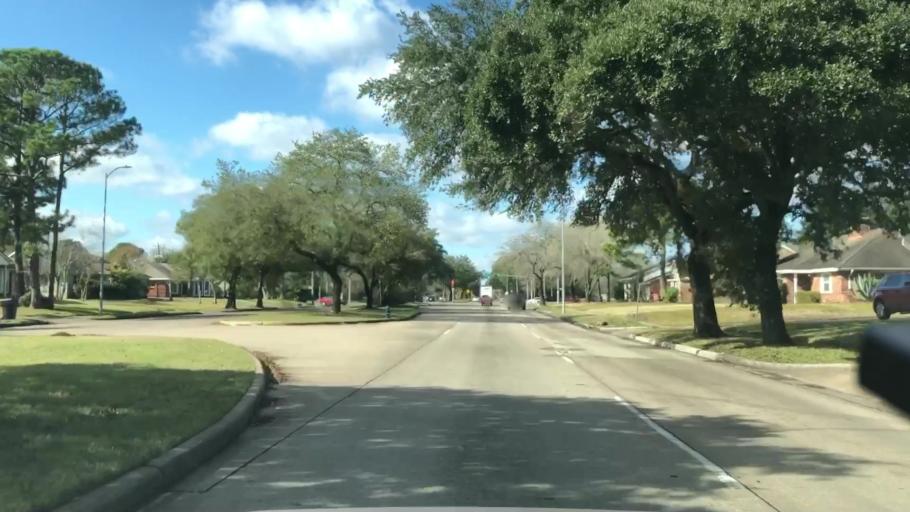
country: US
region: Texas
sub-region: Harris County
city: Bellaire
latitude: 29.6573
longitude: -95.4905
